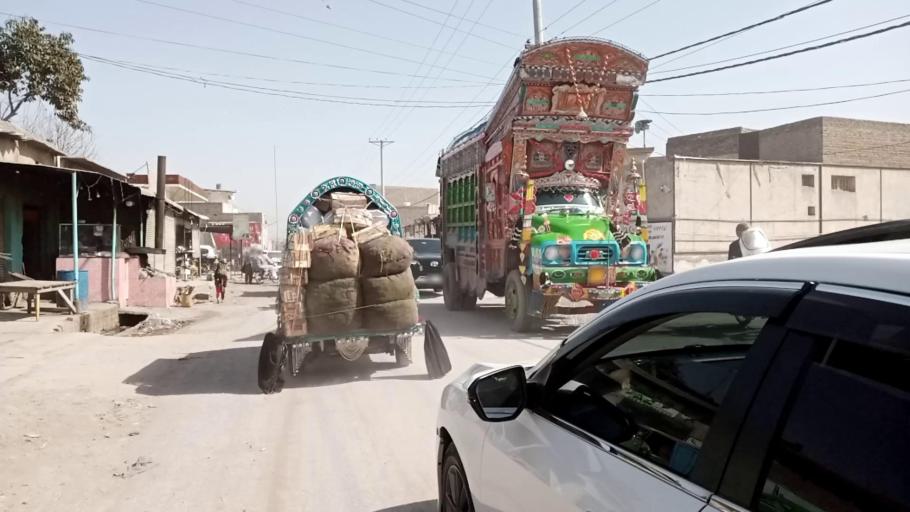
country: PK
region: Khyber Pakhtunkhwa
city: Peshawar
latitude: 34.0070
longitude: 71.6421
